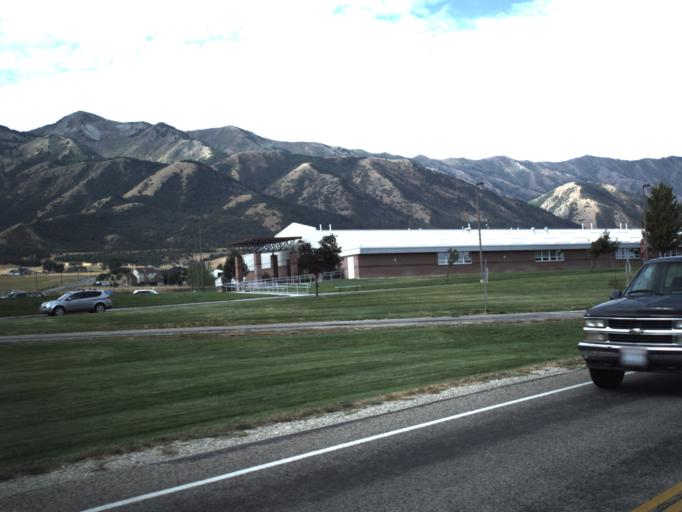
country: US
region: Utah
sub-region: Cache County
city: Wellsville
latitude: 41.6493
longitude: -111.9389
